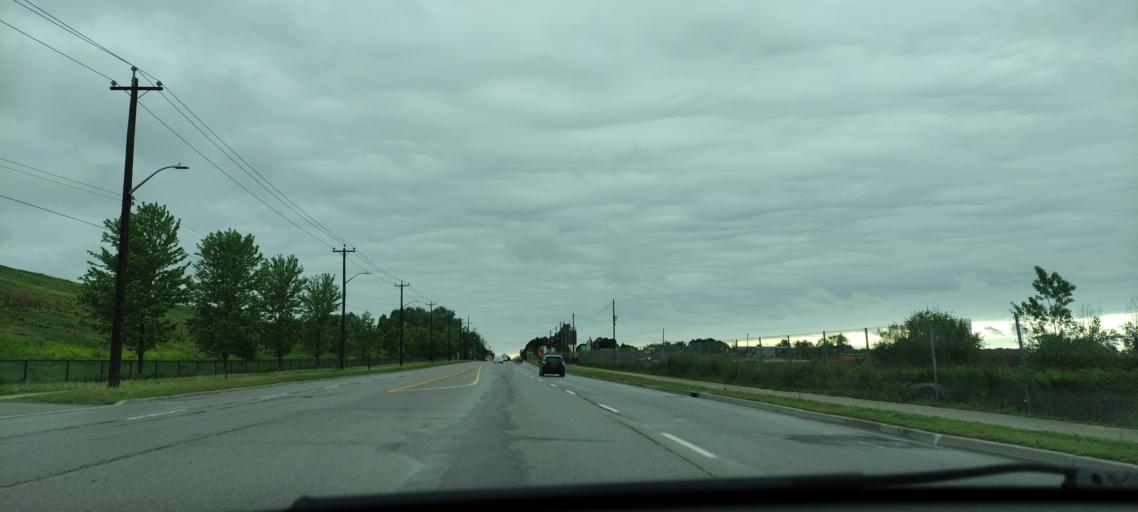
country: CA
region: Ontario
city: Kitchener
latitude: 43.4223
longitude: -80.4906
